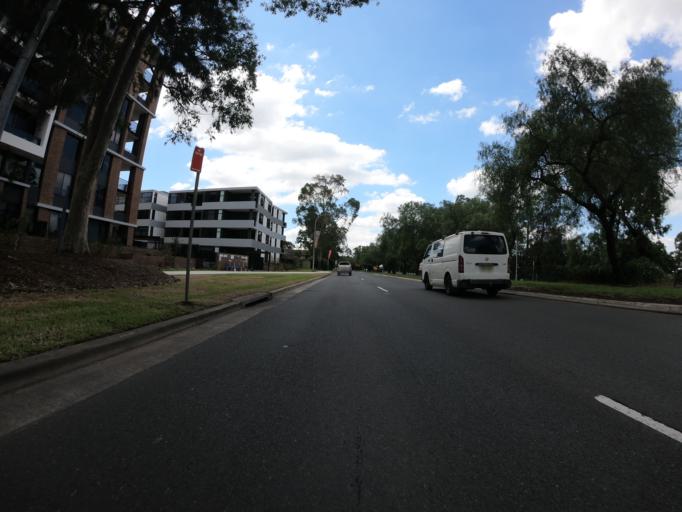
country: AU
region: New South Wales
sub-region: Penrith Municipality
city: Penrith
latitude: -33.7568
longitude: 150.6862
